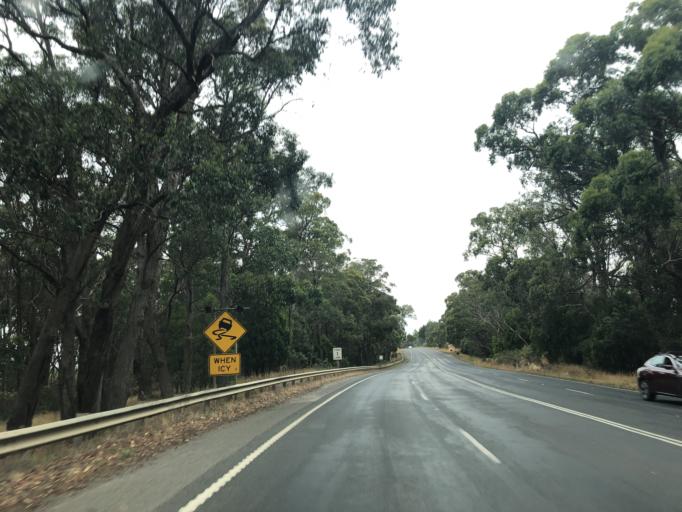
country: AU
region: Victoria
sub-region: Hume
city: Sunbury
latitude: -37.4050
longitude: 144.5376
